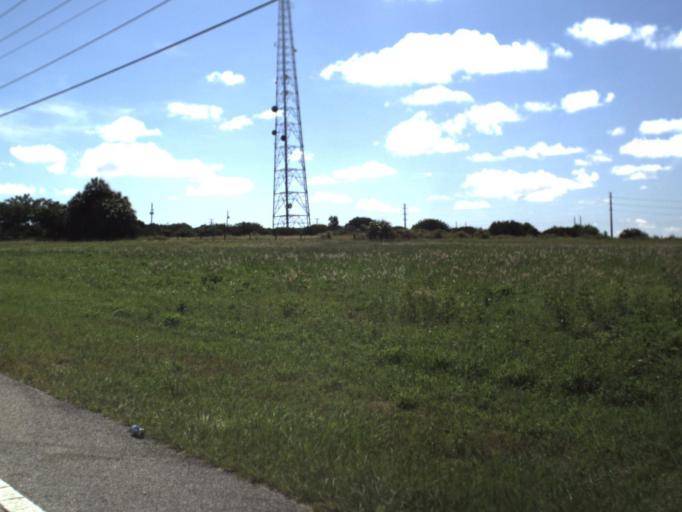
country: US
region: Florida
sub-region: Polk County
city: Dundee
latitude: 28.0124
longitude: -81.6019
